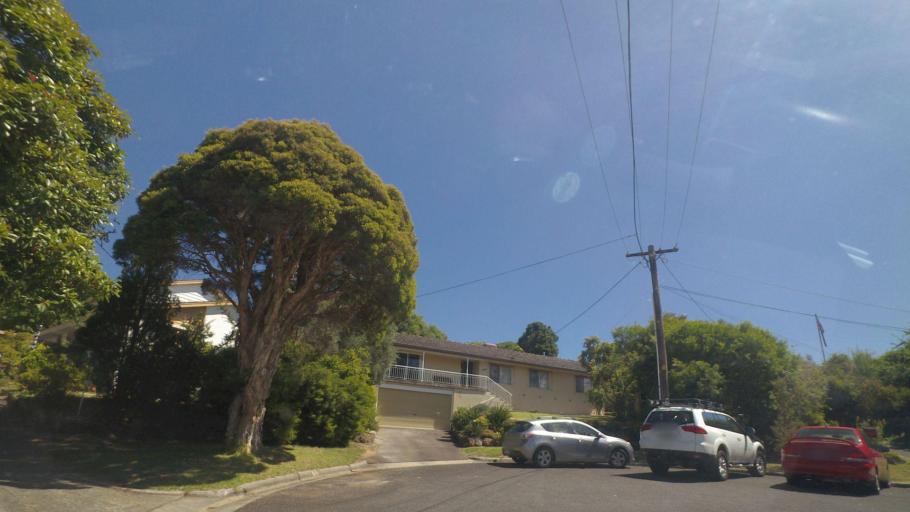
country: AU
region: Victoria
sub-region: Manningham
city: Park Orchards
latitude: -37.7956
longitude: 145.2306
